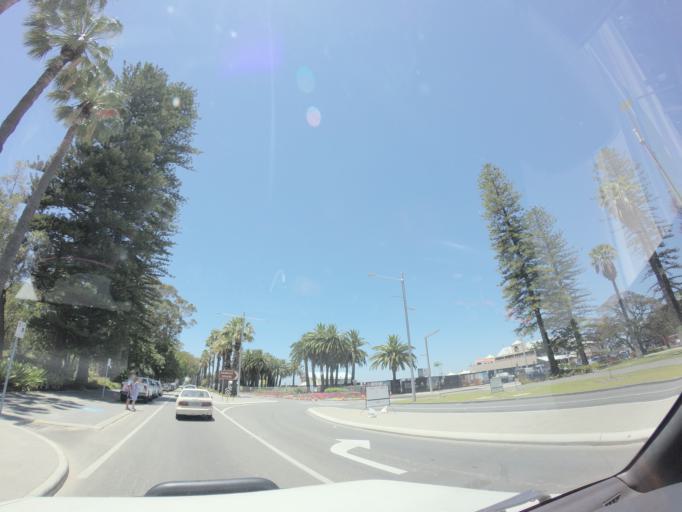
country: AU
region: Western Australia
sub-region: Cambridge
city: Perth
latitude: -31.9587
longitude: 115.8588
